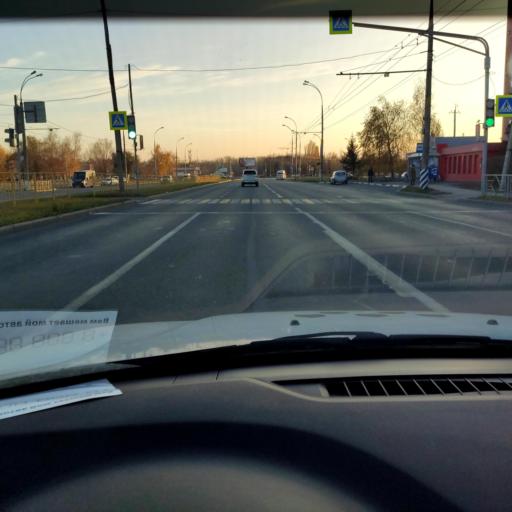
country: RU
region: Samara
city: Tol'yatti
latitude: 53.5006
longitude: 49.2902
